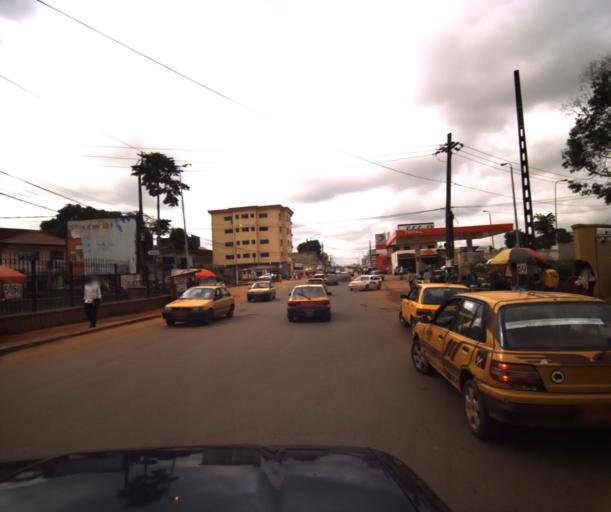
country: CM
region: Centre
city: Yaounde
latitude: 3.8582
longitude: 11.5220
